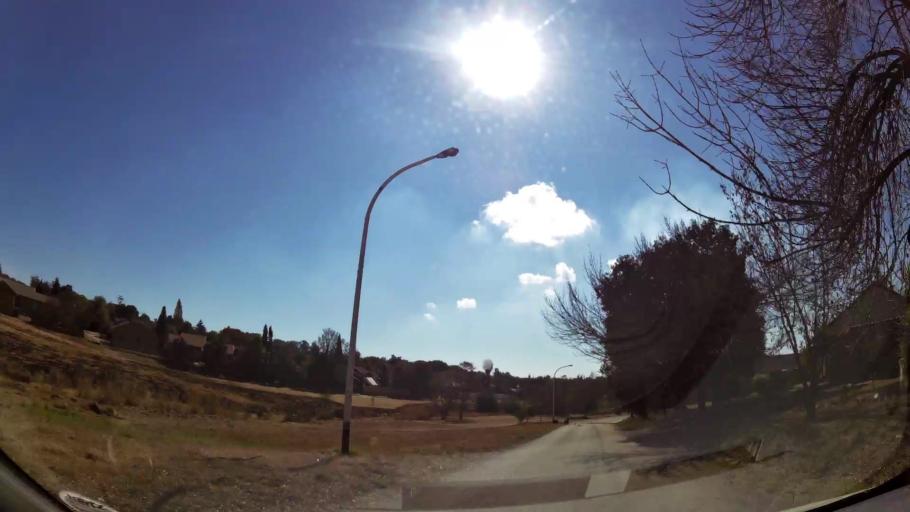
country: ZA
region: Mpumalanga
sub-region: Nkangala District Municipality
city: Witbank
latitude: -25.8509
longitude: 29.2427
